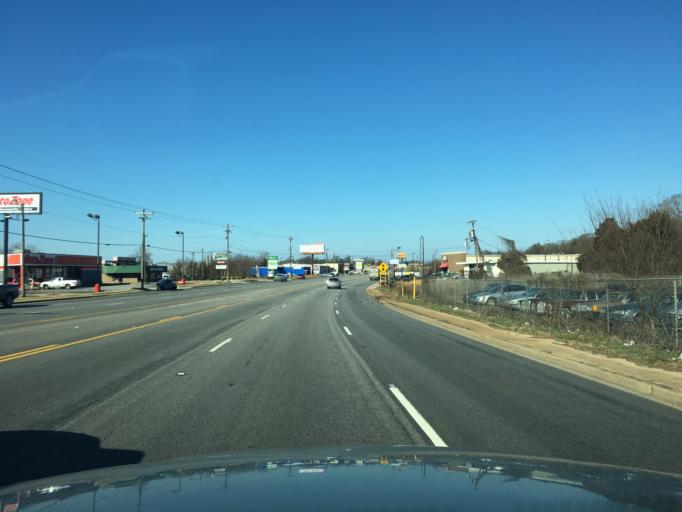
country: US
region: South Carolina
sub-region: Greenville County
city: Sans Souci
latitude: 34.8871
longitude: -82.3951
